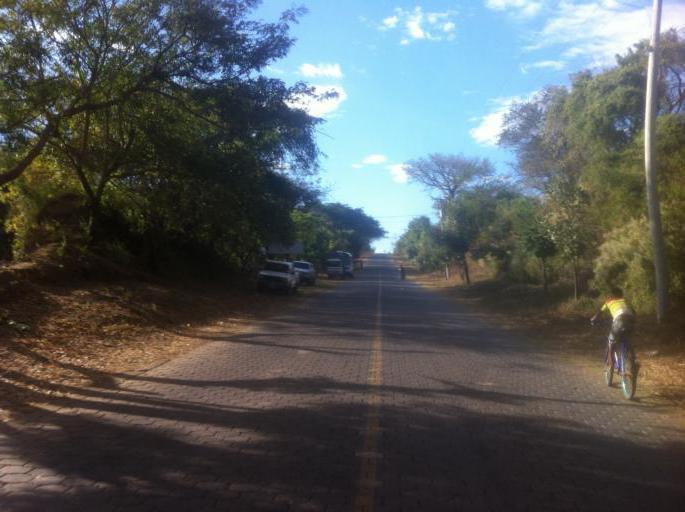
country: NI
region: Managua
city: Masachapa
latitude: 11.8195
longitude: -86.4962
